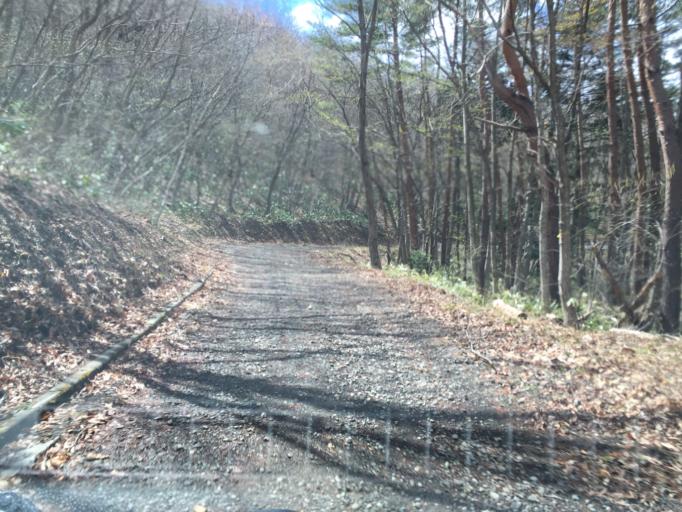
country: JP
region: Fukushima
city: Fukushima-shi
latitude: 37.8588
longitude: 140.4202
